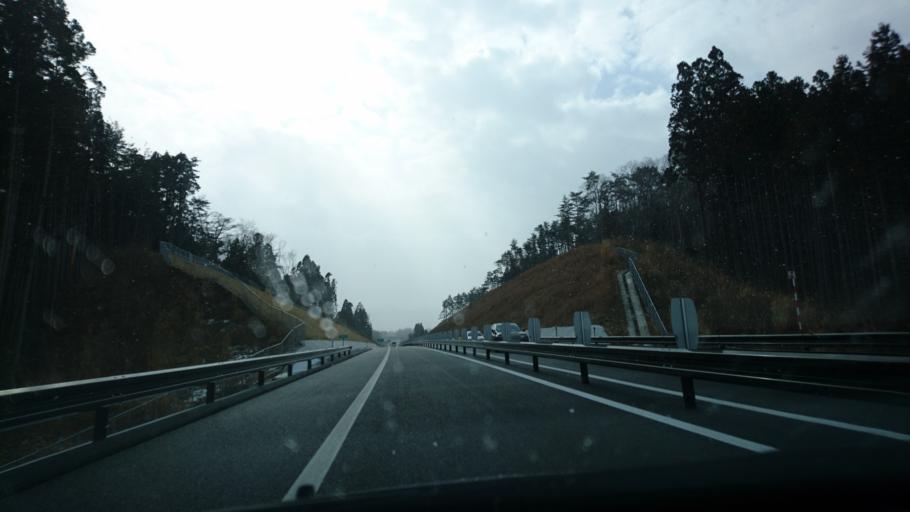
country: JP
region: Iwate
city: Ofunato
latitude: 38.7982
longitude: 141.5294
